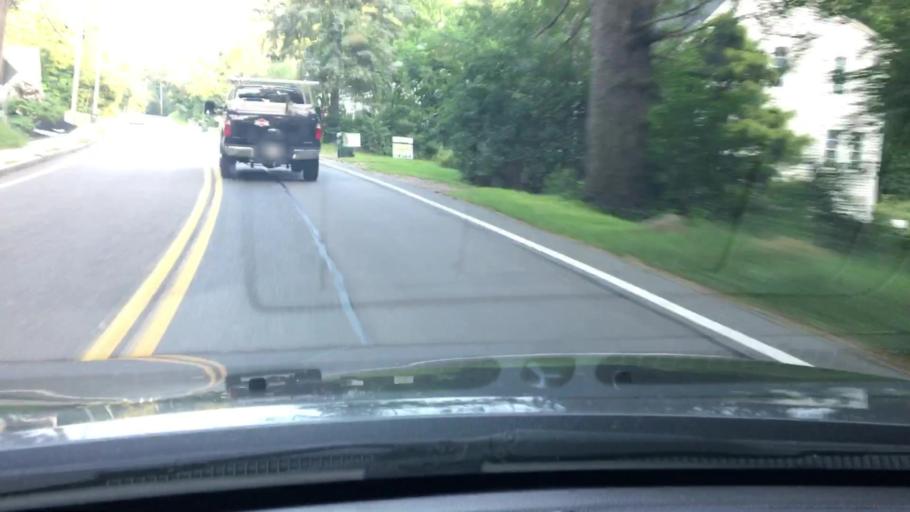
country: US
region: Massachusetts
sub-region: Middlesex County
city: Hopkinton
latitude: 42.2363
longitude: -71.5599
